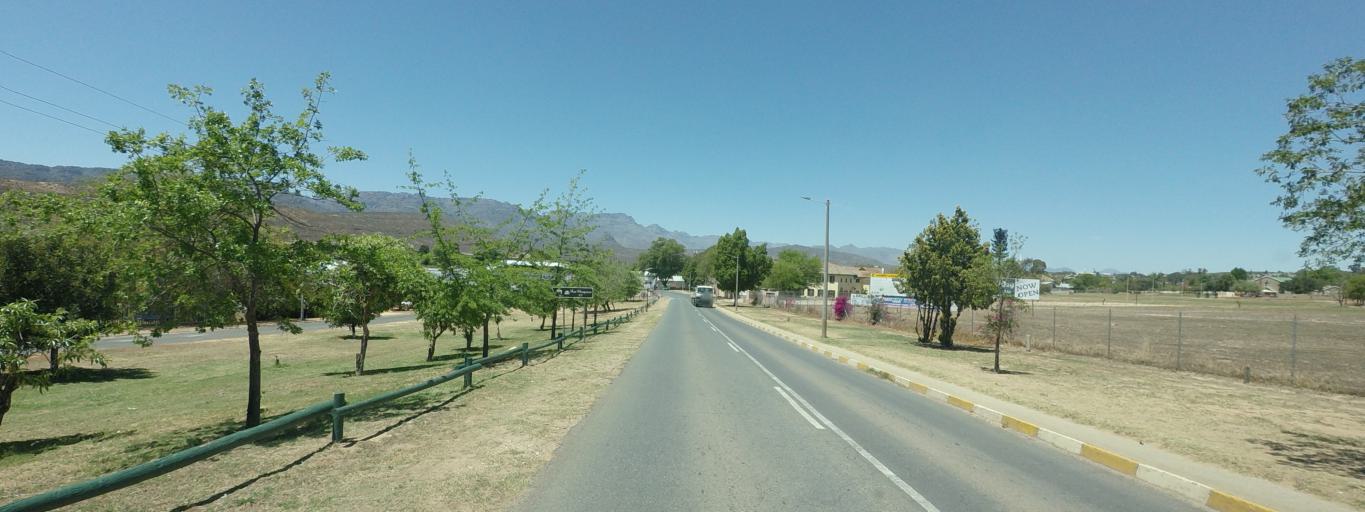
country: ZA
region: Western Cape
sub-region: West Coast District Municipality
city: Clanwilliam
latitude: -32.1749
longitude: 18.8889
